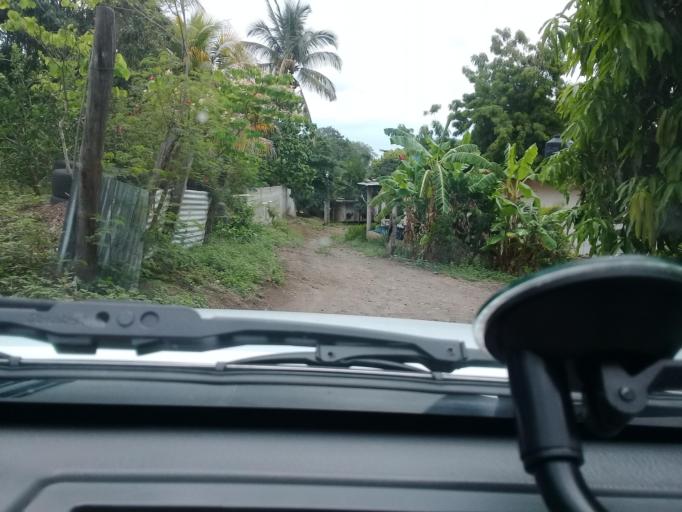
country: MX
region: Veracruz
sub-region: Paso de Ovejas
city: El Hatito
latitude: 19.2795
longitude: -96.3895
